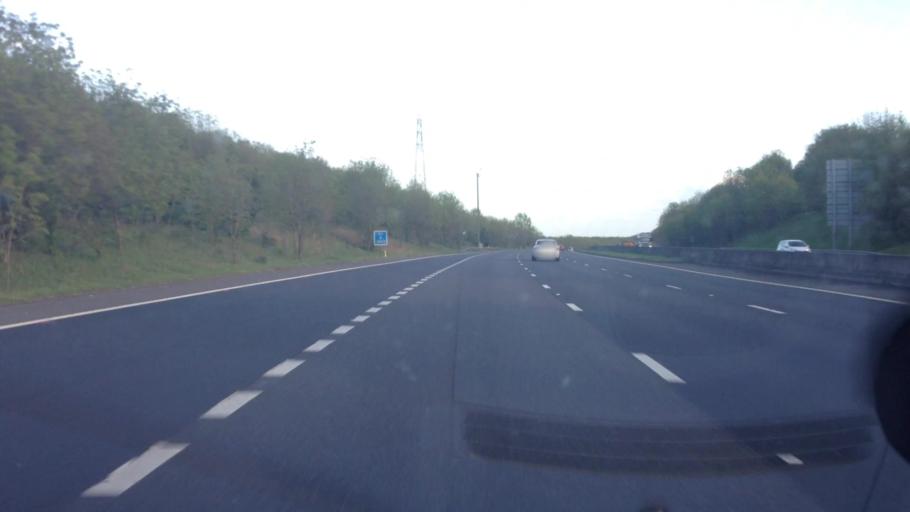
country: GB
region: England
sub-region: Barnsley
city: Birdwell
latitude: 53.4932
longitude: -1.4716
